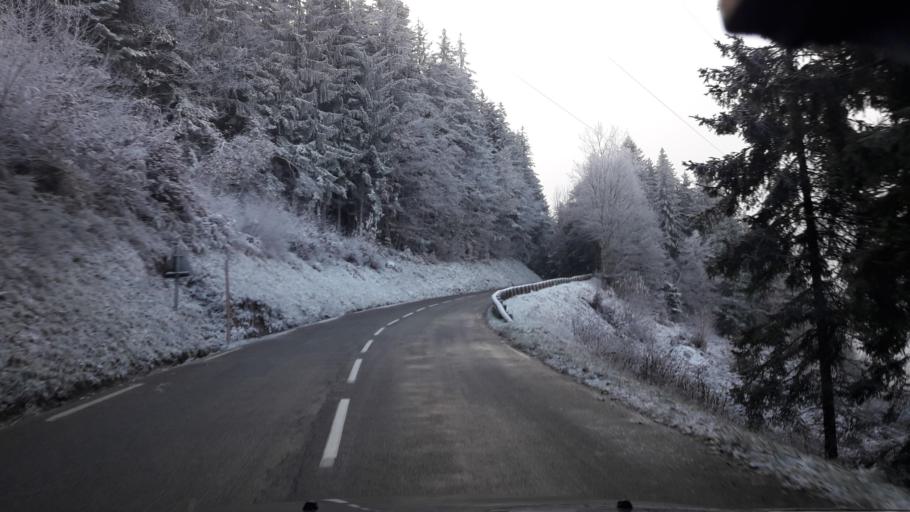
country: FR
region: Rhone-Alpes
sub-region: Departement de l'Isere
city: Allevard
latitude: 45.3904
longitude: 6.0929
